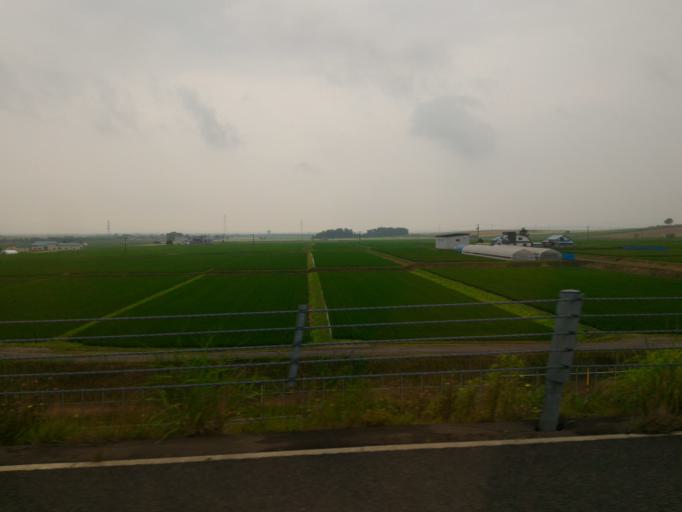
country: JP
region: Hokkaido
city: Fukagawa
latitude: 43.8003
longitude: 141.9031
